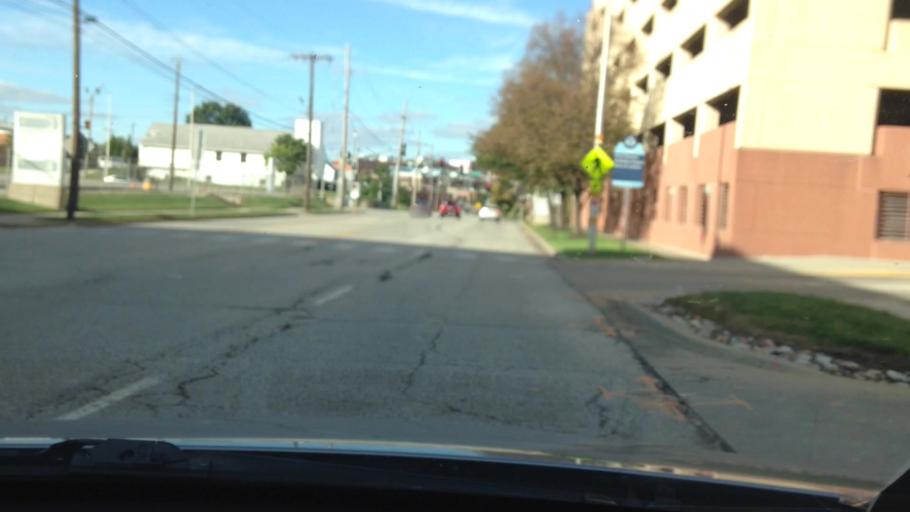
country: US
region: Kansas
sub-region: Johnson County
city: Westwood
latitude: 39.0484
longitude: -94.5920
